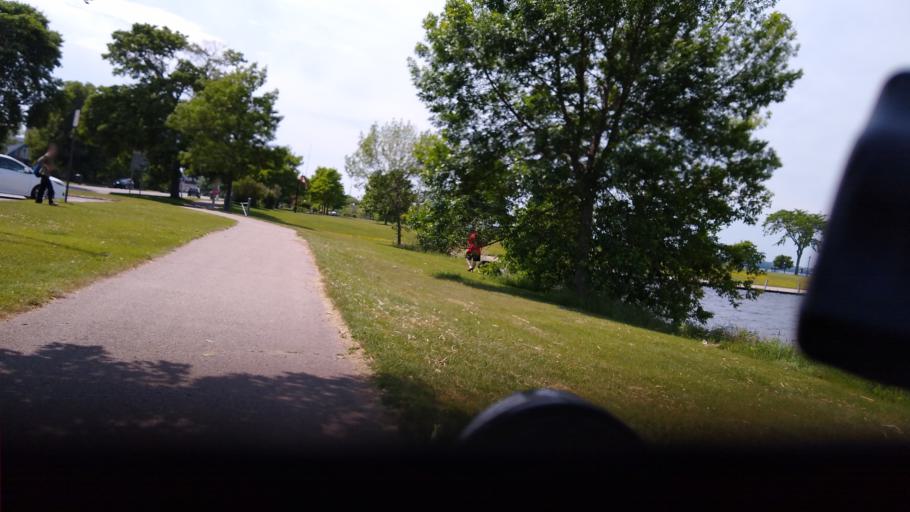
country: US
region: Michigan
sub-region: Delta County
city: Escanaba
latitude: 45.7454
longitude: -87.0460
